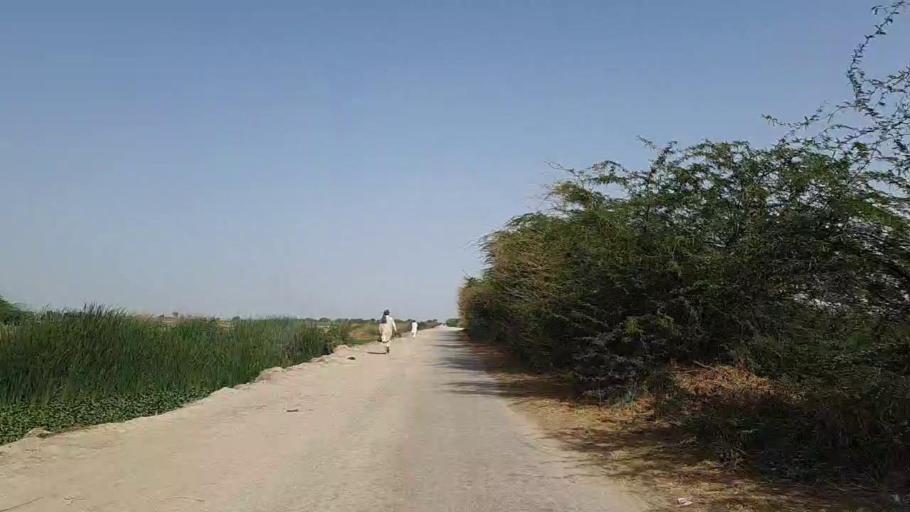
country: PK
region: Sindh
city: Jati
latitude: 24.3606
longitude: 68.2722
